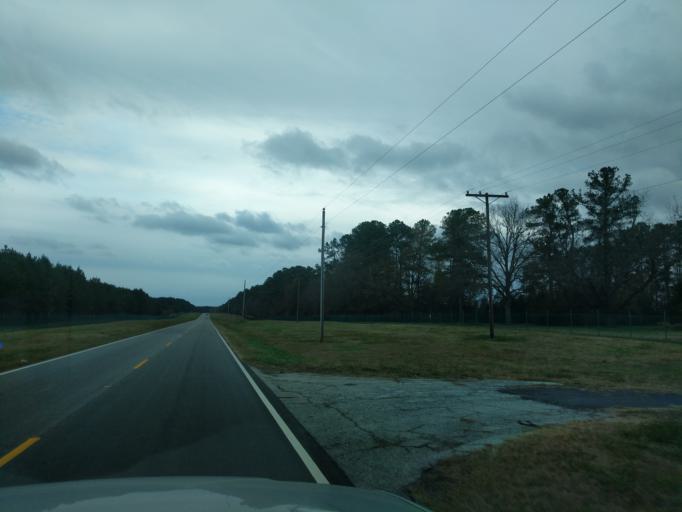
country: US
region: South Carolina
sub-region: Laurens County
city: Laurens
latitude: 34.4141
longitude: -82.0408
